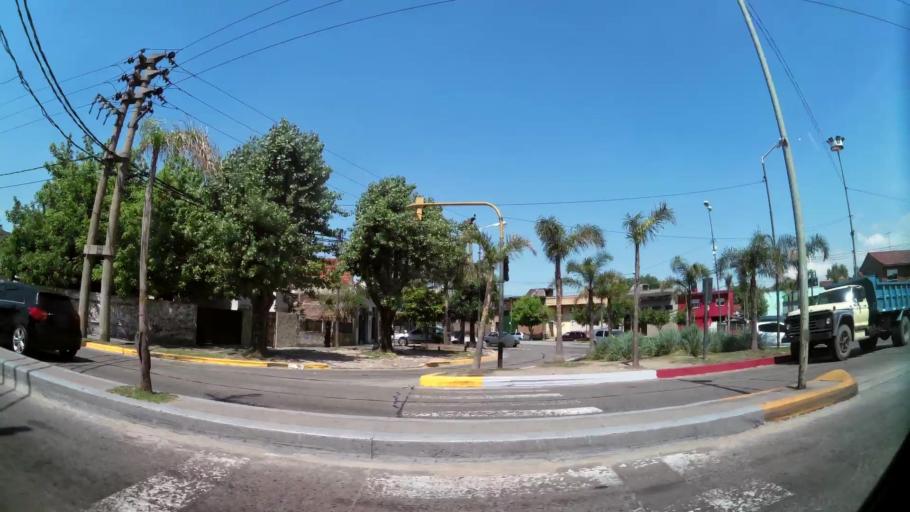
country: AR
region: Buenos Aires
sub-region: Partido de Tigre
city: Tigre
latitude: -34.4720
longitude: -58.5971
